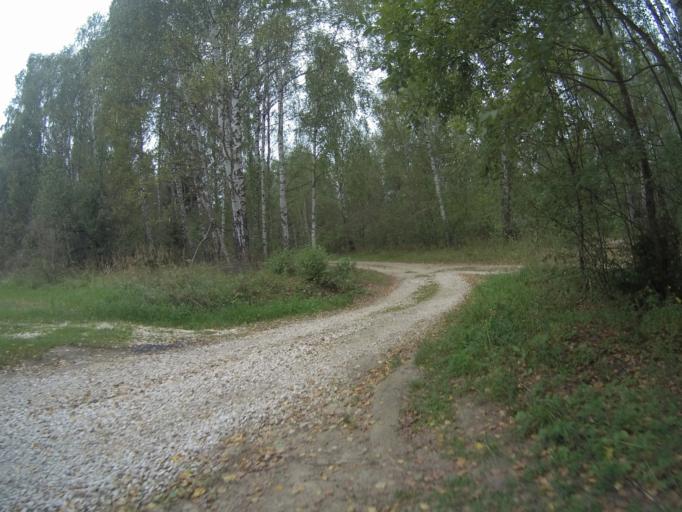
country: RU
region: Vladimir
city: Golovino
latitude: 55.9738
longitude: 40.4647
